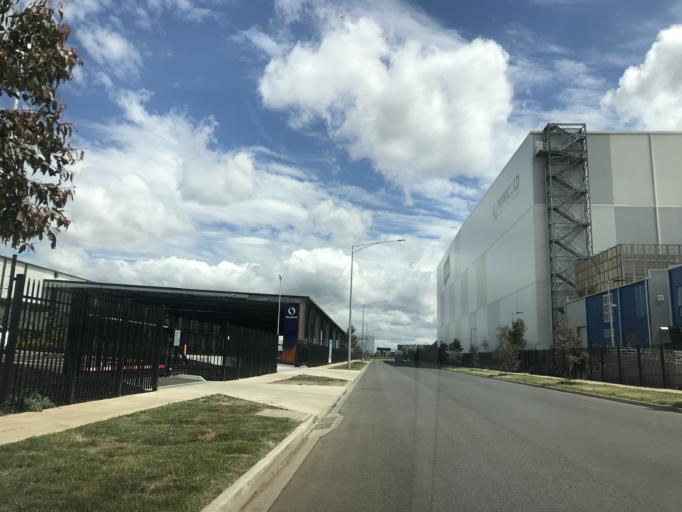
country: AU
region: Victoria
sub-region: Wyndham
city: Truganina
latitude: -37.7992
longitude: 144.7486
